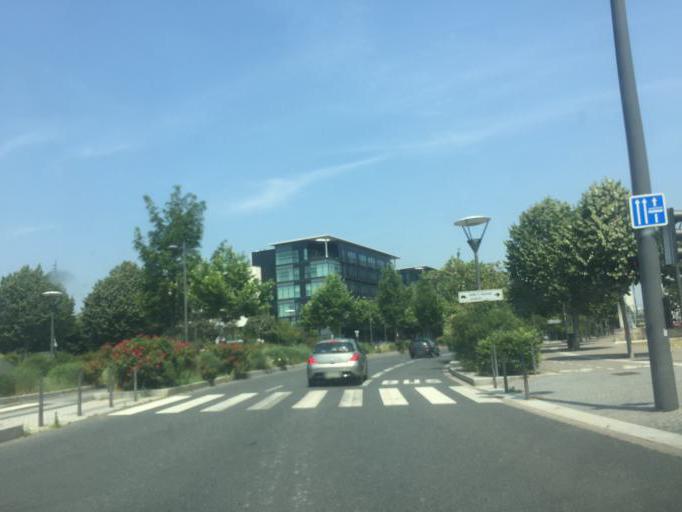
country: FR
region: Rhone-Alpes
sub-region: Departement du Rhone
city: La Mulatiere
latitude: 45.7280
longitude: 4.8242
